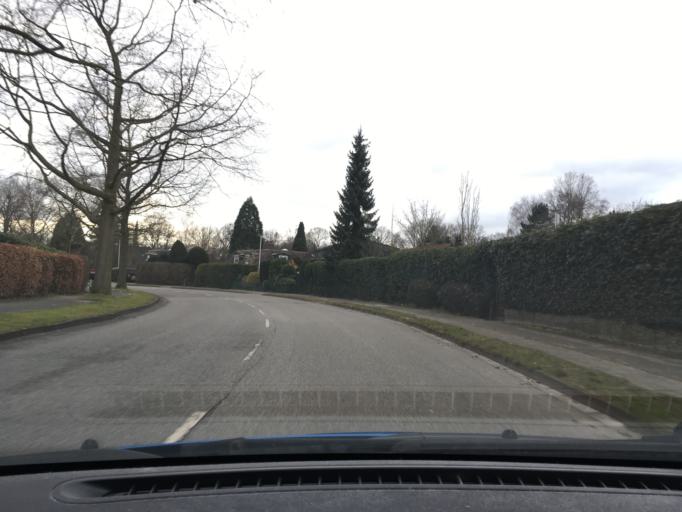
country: DE
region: Schleswig-Holstein
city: Wedel
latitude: 53.5914
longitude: 9.7193
